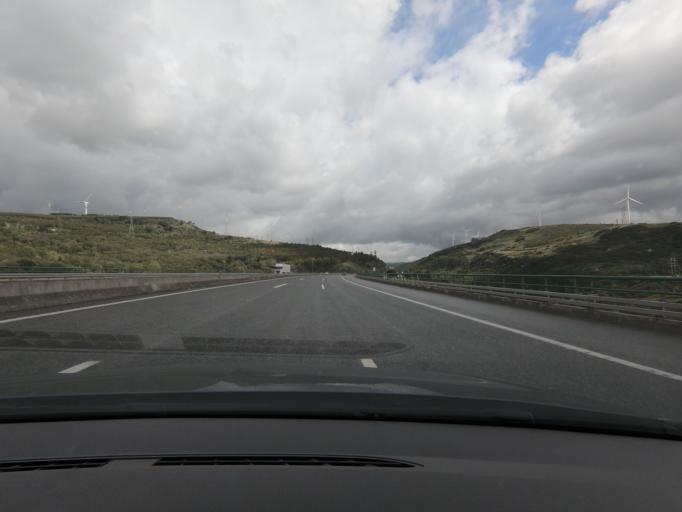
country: PT
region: Lisbon
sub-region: Loures
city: Santo Antao do Tojal
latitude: 38.8738
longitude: -9.1344
